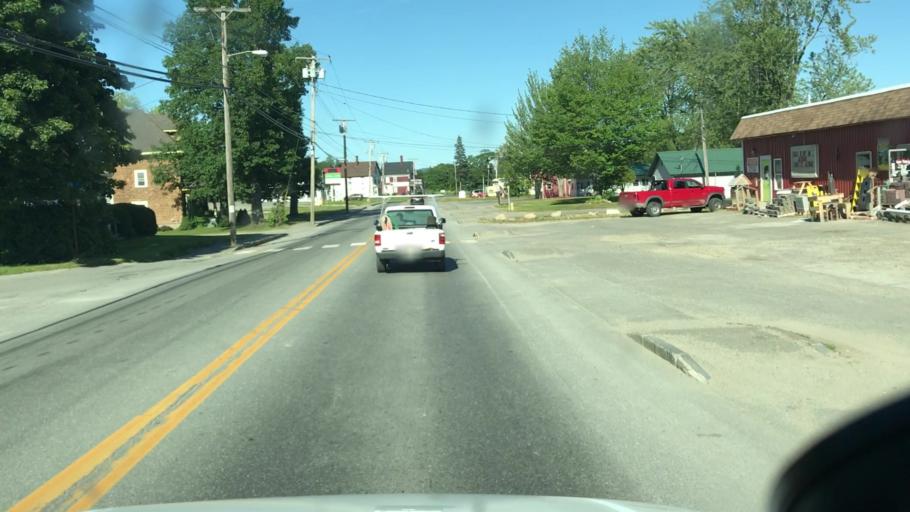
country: US
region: Maine
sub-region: Penobscot County
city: Lincoln
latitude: 45.3627
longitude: -68.5145
